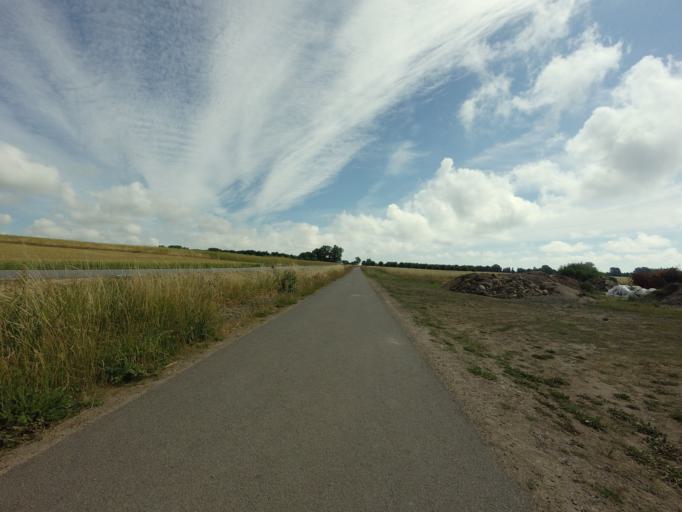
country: SE
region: Skane
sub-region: Simrishamns Kommun
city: Simrishamn
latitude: 55.4842
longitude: 14.2882
